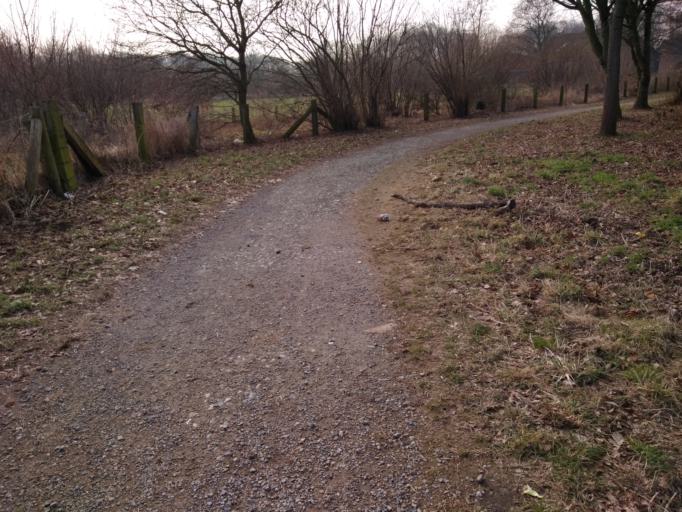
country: DE
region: North Rhine-Westphalia
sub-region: Regierungsbezirk Munster
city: Gladbeck
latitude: 51.5897
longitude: 7.0146
